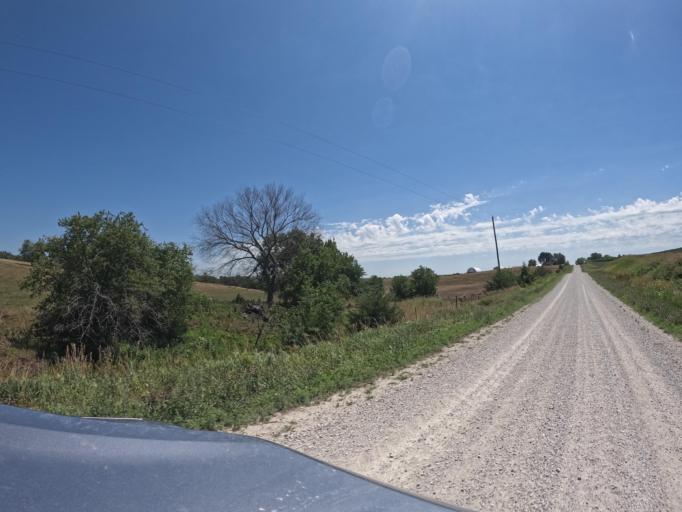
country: US
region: Iowa
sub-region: Keokuk County
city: Sigourney
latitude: 41.4186
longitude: -92.3162
